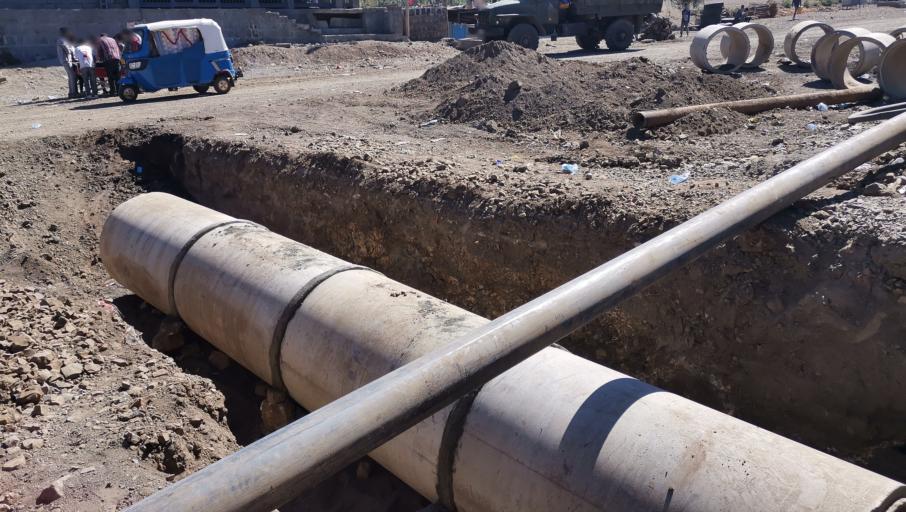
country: ET
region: Tigray
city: Korem
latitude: 12.6225
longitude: 39.0361
